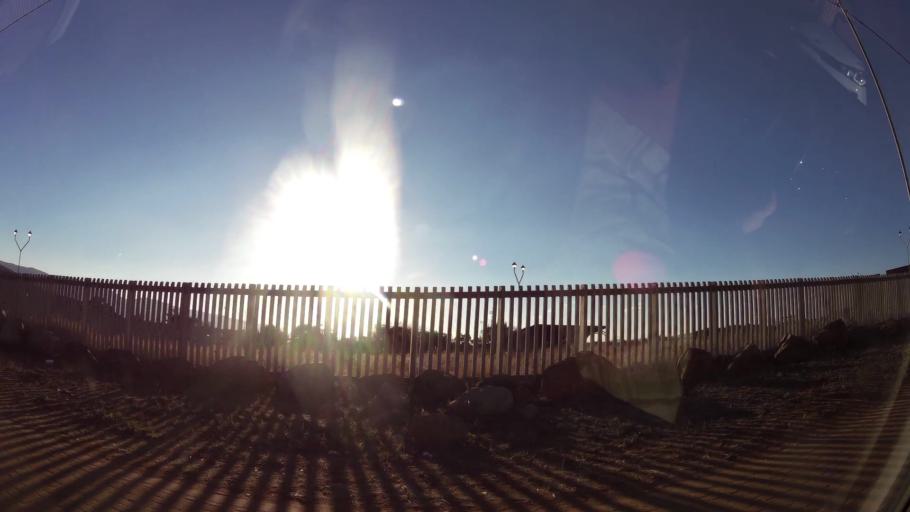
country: ZA
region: Limpopo
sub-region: Waterberg District Municipality
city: Mokopane
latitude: -24.1454
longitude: 28.9891
